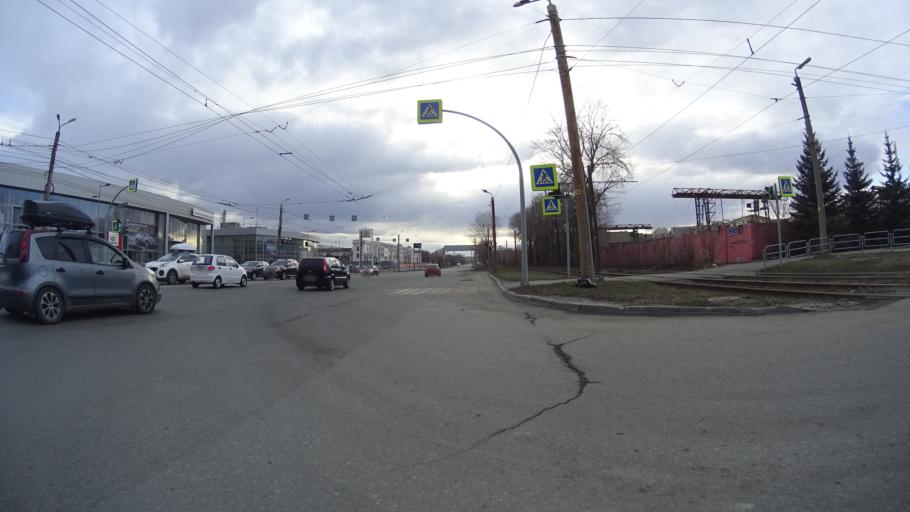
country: RU
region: Chelyabinsk
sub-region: Gorod Chelyabinsk
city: Chelyabinsk
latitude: 55.1594
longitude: 61.4648
